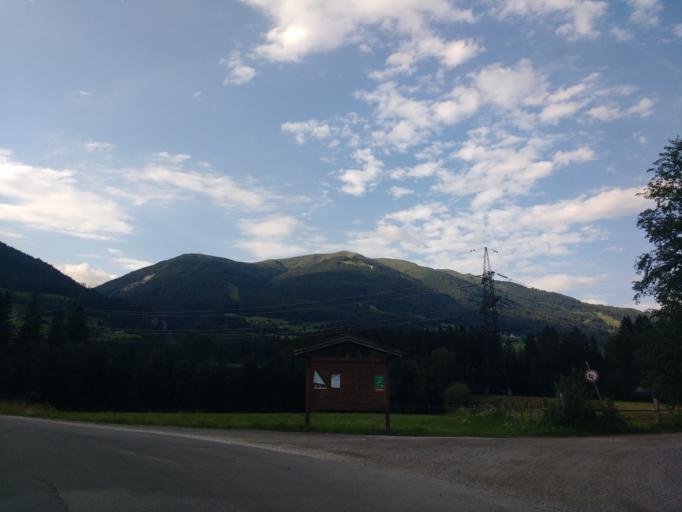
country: AT
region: Salzburg
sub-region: Politischer Bezirk Zell am See
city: Neukirchen am Grossvenediger
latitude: 47.2438
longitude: 12.2632
